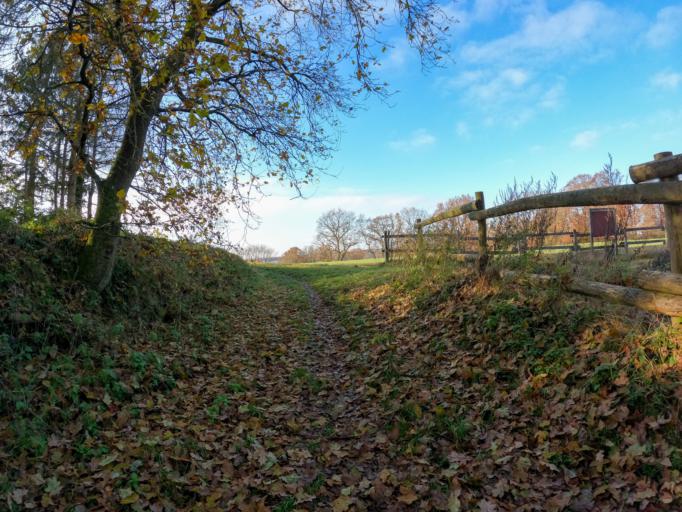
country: LU
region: Luxembourg
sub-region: Canton de Capellen
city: Mamer
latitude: 49.6426
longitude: 6.0222
